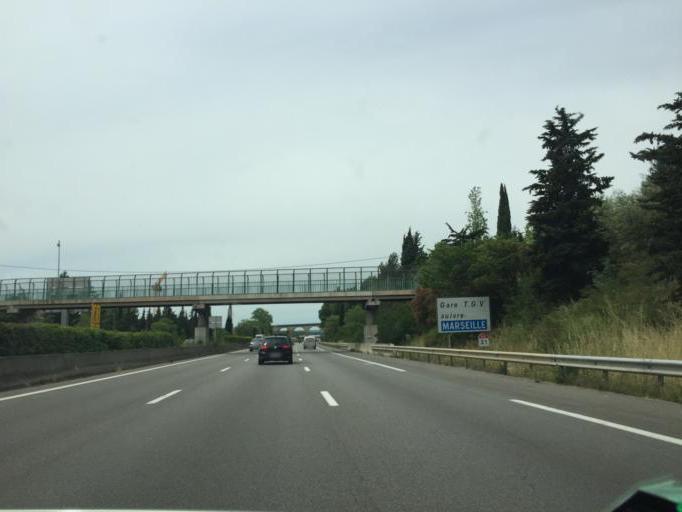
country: FR
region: Provence-Alpes-Cote d'Azur
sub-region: Departement des Bouches-du-Rhone
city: Aix-en-Provence
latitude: 43.5124
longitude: 5.4622
